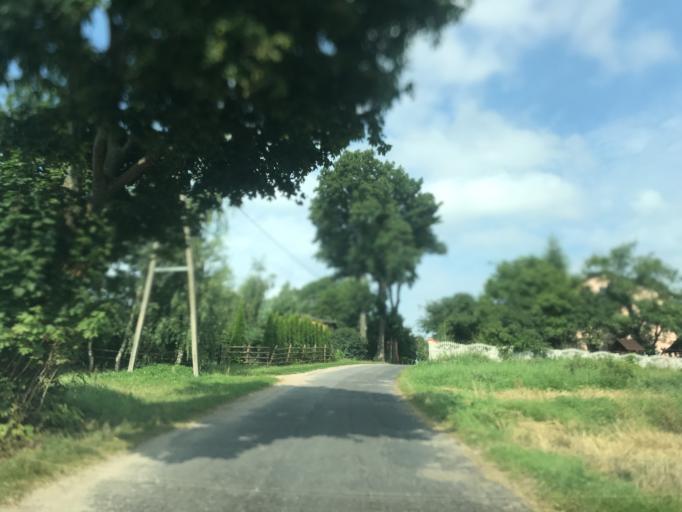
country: PL
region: Warmian-Masurian Voivodeship
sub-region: Powiat nowomiejski
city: Biskupiec
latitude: 53.4203
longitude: 19.4448
